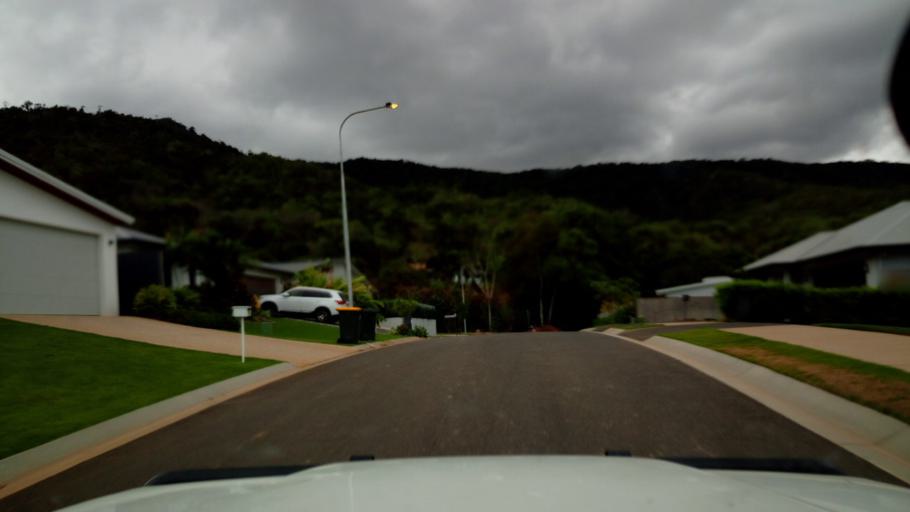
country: AU
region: Queensland
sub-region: Cairns
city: Redlynch
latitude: -16.8445
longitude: 145.6891
